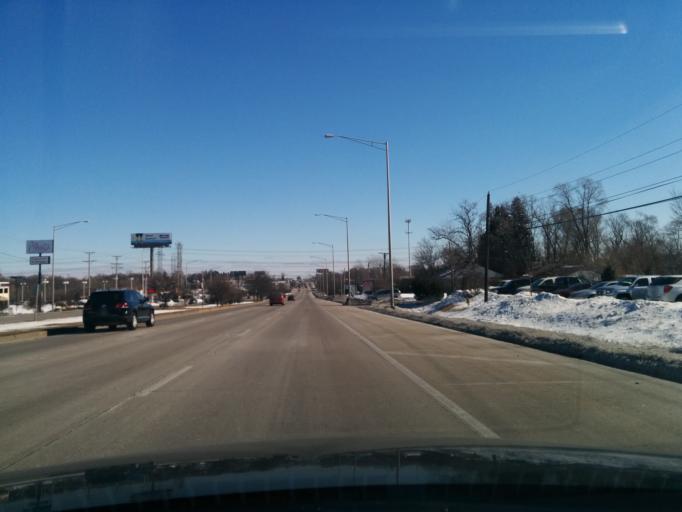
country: US
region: Illinois
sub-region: DuPage County
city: Glendale Heights
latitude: 41.9036
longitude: -88.0541
